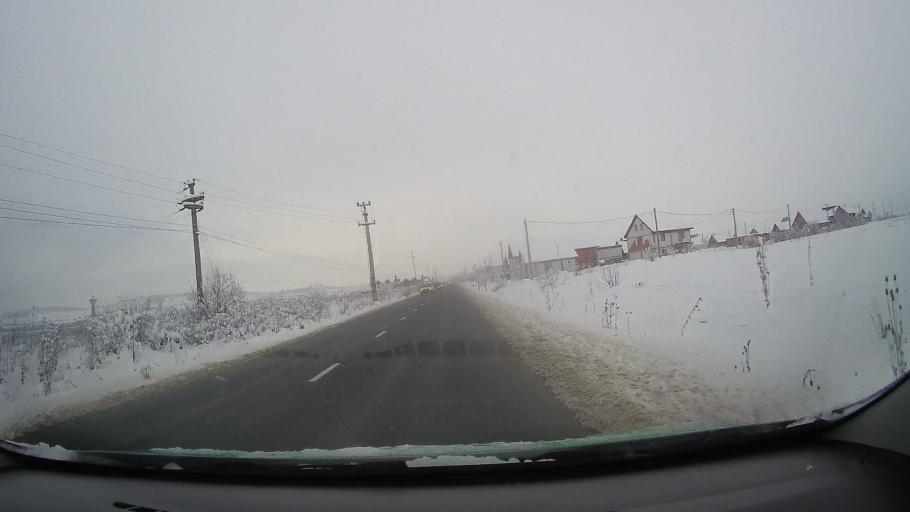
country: RO
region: Sibiu
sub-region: Comuna Cristian
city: Cristian
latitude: 45.7725
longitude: 24.0195
